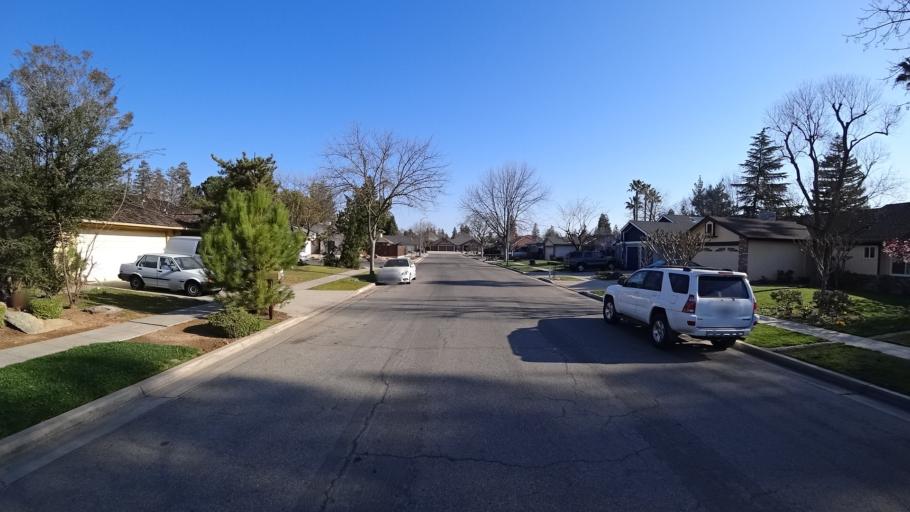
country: US
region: California
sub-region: Fresno County
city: Clovis
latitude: 36.8566
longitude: -119.7961
